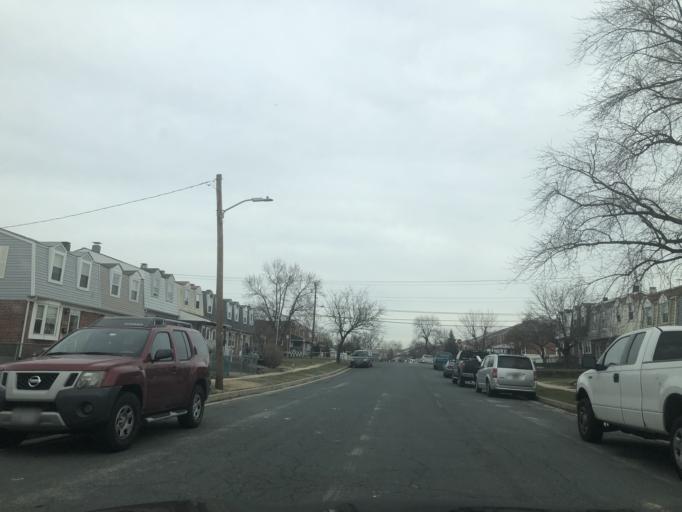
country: US
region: Maryland
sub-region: Baltimore County
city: Dundalk
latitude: 39.2614
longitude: -76.4939
